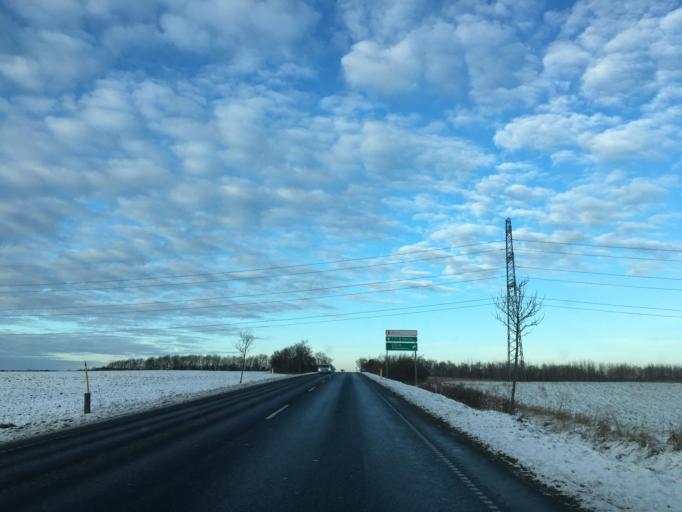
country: DK
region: Zealand
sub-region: Koge Kommune
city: Borup
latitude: 55.4543
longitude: 11.9849
